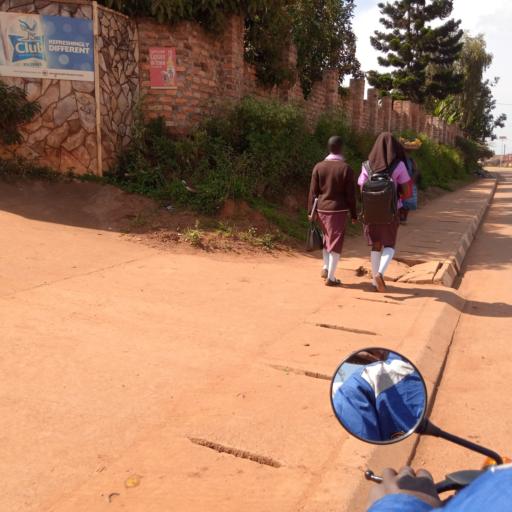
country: UG
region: Central Region
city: Masaka
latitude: -0.3459
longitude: 31.7314
